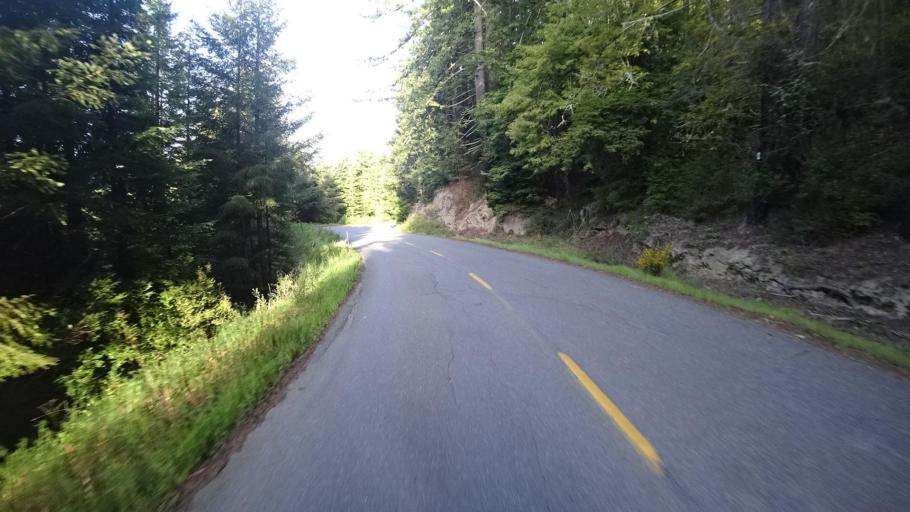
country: US
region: California
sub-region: Humboldt County
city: Bayside
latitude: 40.7550
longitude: -124.0423
